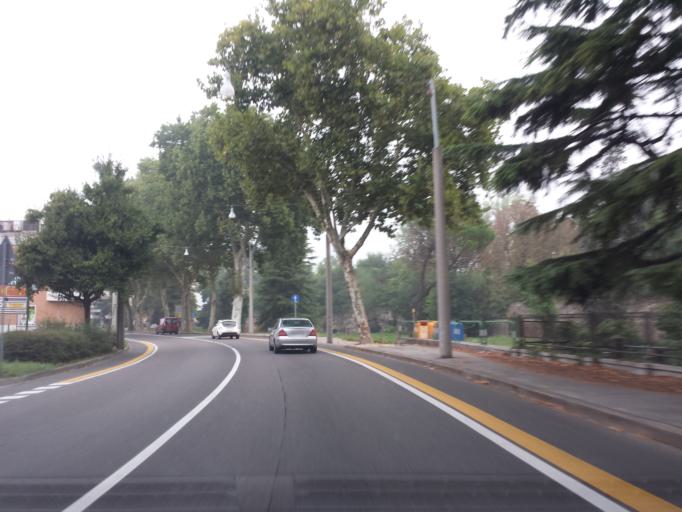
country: IT
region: Veneto
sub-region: Provincia di Padova
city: Padova
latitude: 45.4150
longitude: 11.8643
